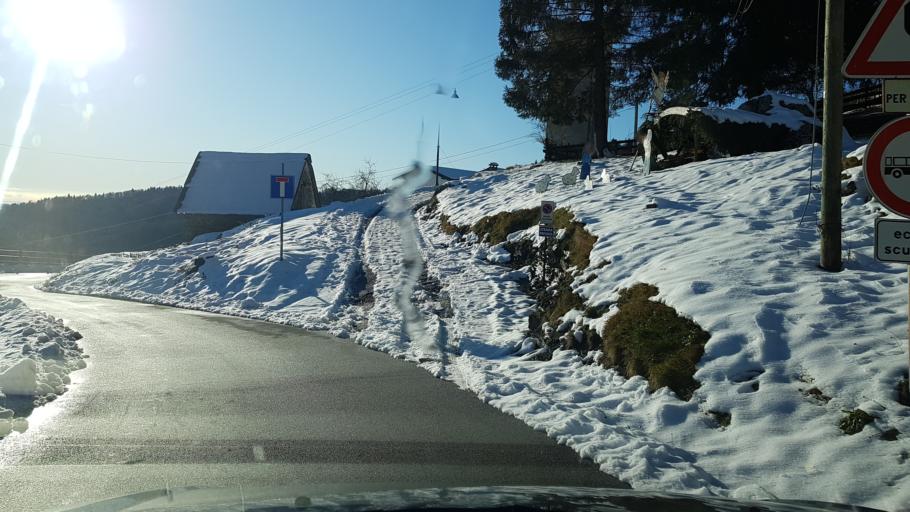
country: IT
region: Friuli Venezia Giulia
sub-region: Provincia di Udine
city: Savogna
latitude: 46.1949
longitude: 13.5300
